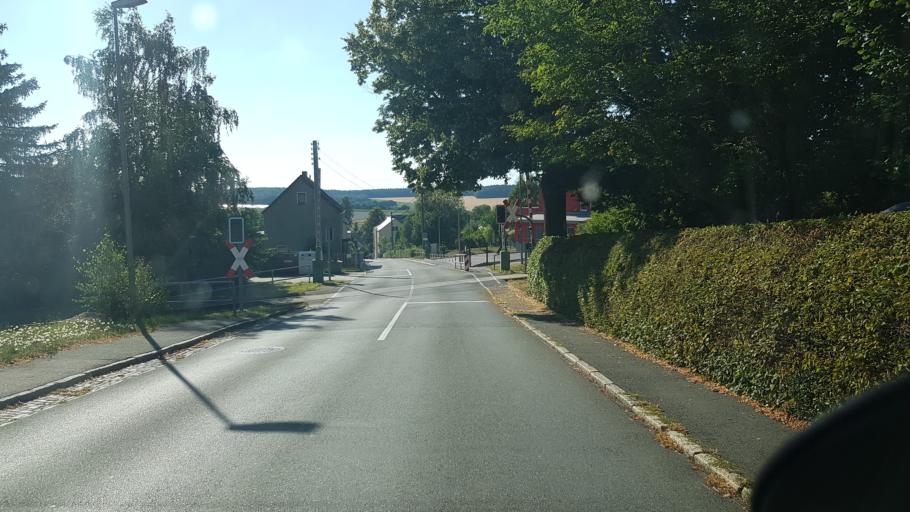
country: DE
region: Saxony
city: Hirschfeld
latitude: 50.6508
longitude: 12.4440
